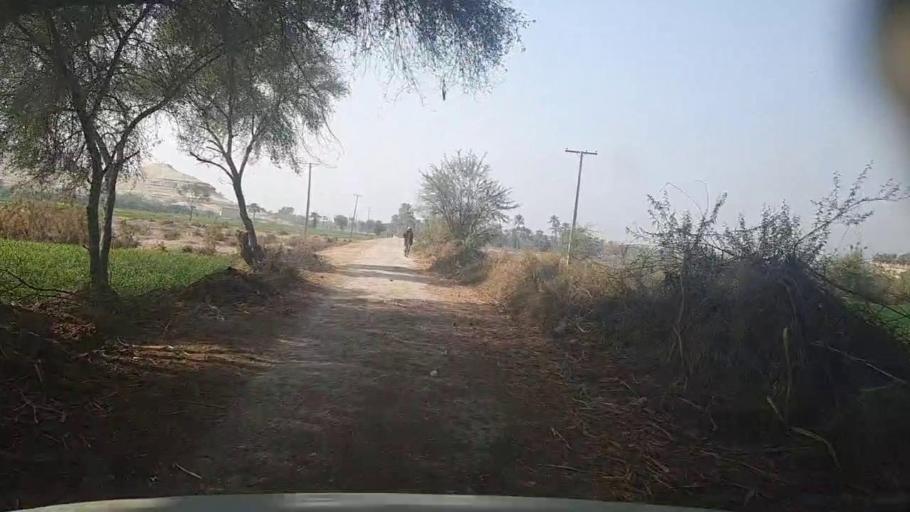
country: PK
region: Sindh
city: Kot Diji
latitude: 27.3482
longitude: 68.7226
